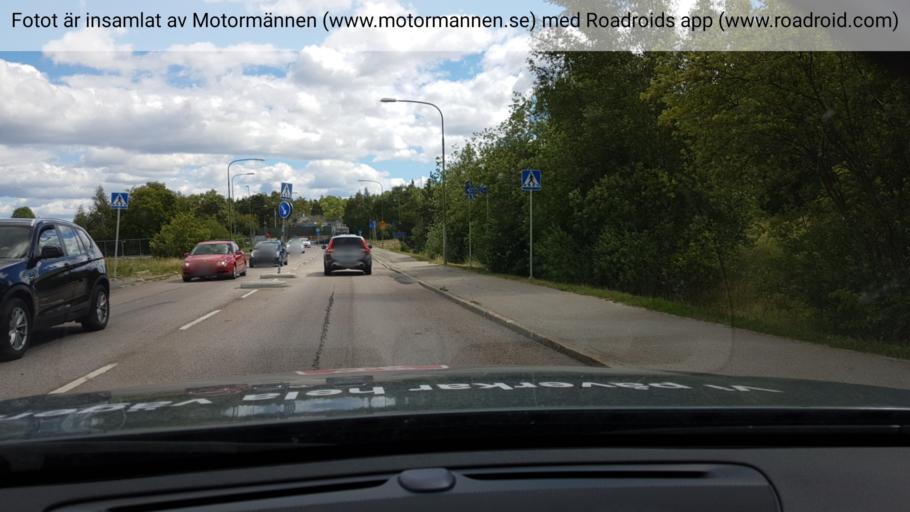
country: SE
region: Stockholm
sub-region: Stockholms Kommun
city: Arsta
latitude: 59.2874
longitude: 18.0428
